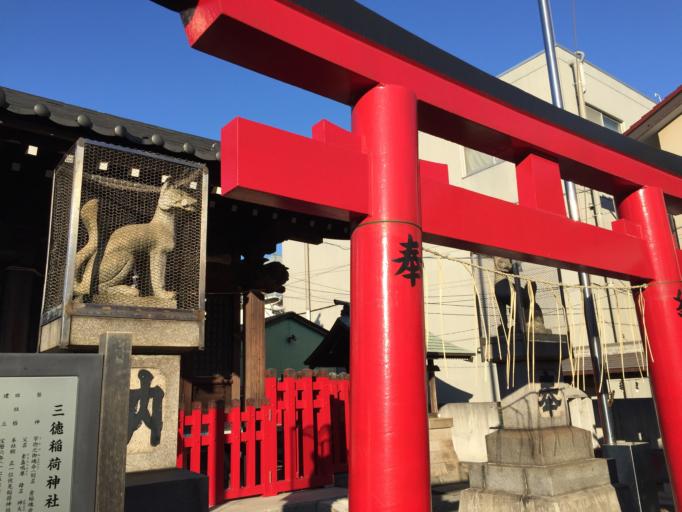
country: JP
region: Kanagawa
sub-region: Kawasaki-shi
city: Kawasaki
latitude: 35.5532
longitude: 139.7358
